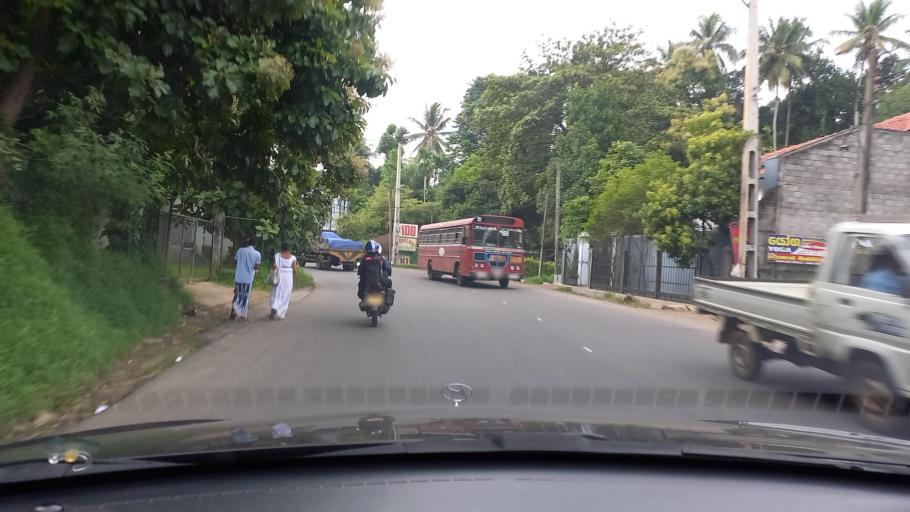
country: LK
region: Central
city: Kadugannawa
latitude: 7.2475
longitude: 80.4646
